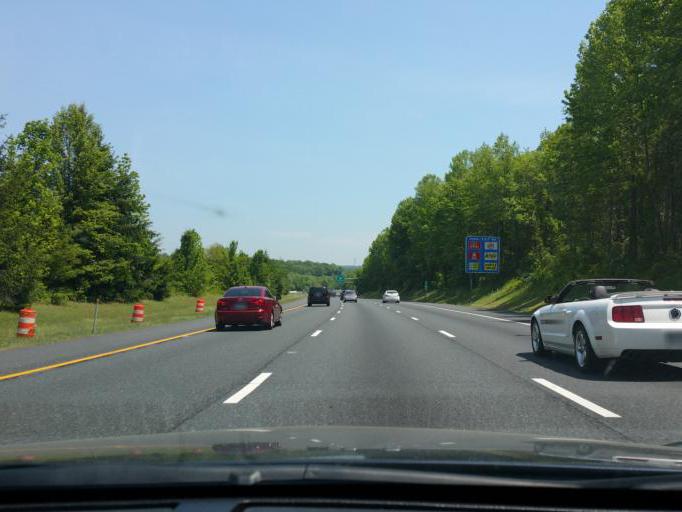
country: US
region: Maryland
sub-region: Harford County
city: Riverside
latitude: 39.4717
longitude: -76.2755
